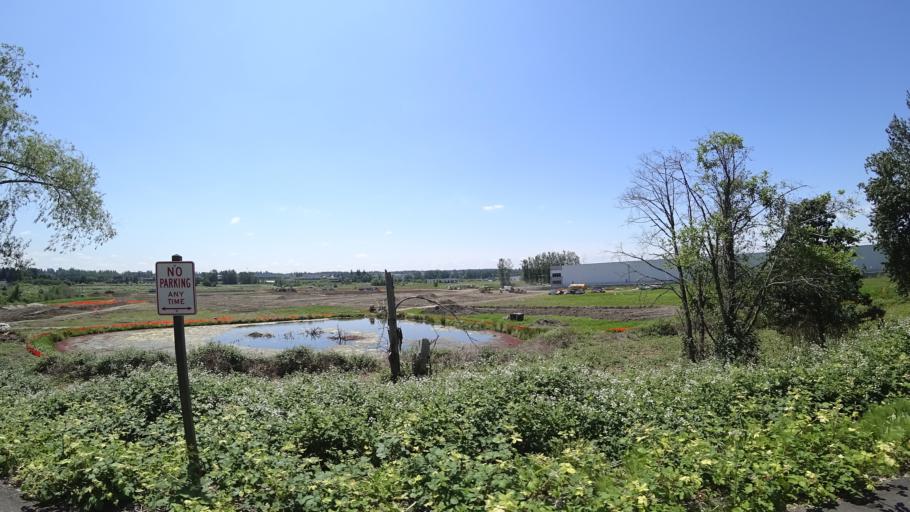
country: US
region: Oregon
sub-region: Multnomah County
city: Fairview
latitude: 45.5548
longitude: -122.4578
